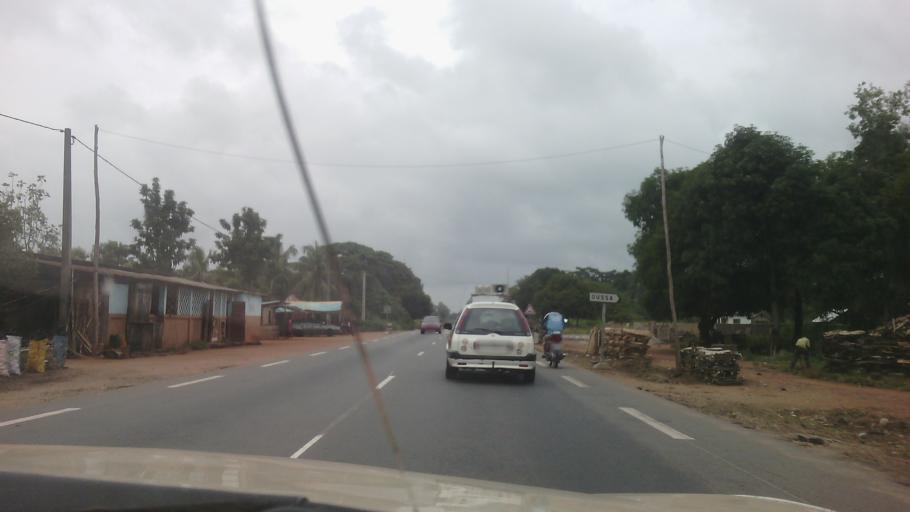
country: BJ
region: Mono
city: Come
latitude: 6.3999
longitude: 1.9749
